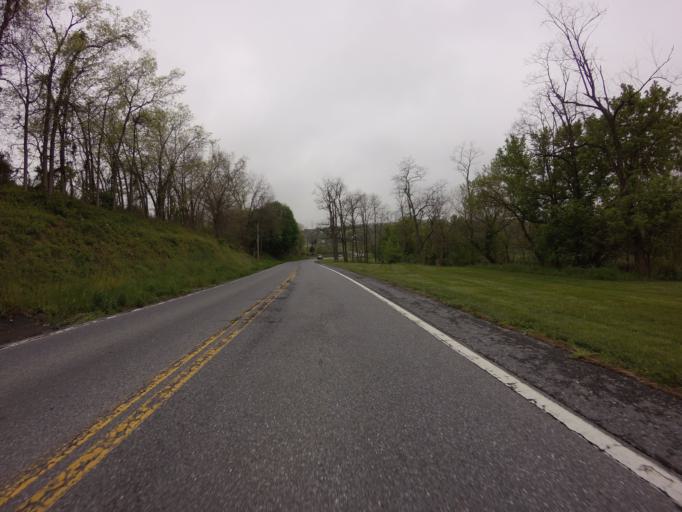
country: US
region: Maryland
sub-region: Frederick County
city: Myersville
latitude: 39.4901
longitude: -77.5678
